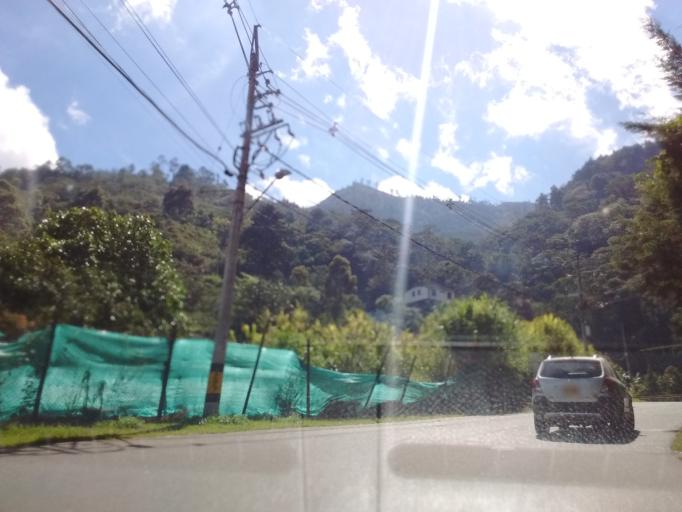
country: CO
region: Antioquia
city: Medellin
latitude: 6.2260
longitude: -75.5149
